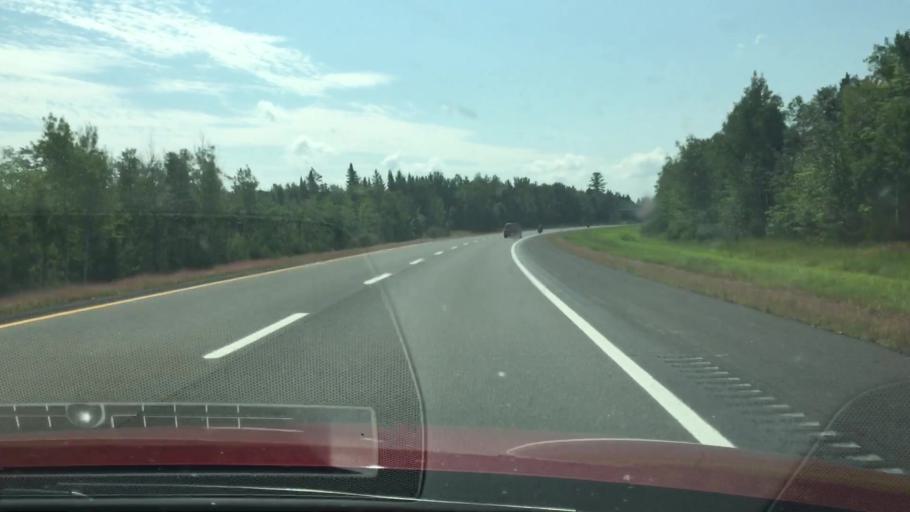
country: US
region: Maine
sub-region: Penobscot County
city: Patten
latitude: 45.9929
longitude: -68.2800
